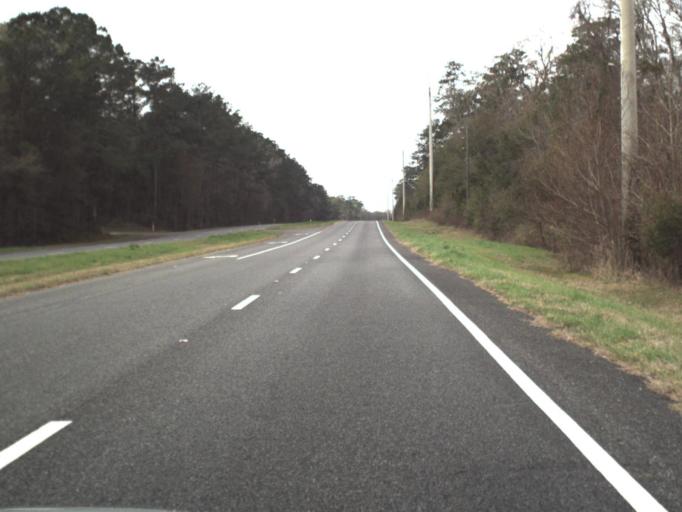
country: US
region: Florida
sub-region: Jefferson County
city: Monticello
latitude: 30.4029
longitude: -84.0418
